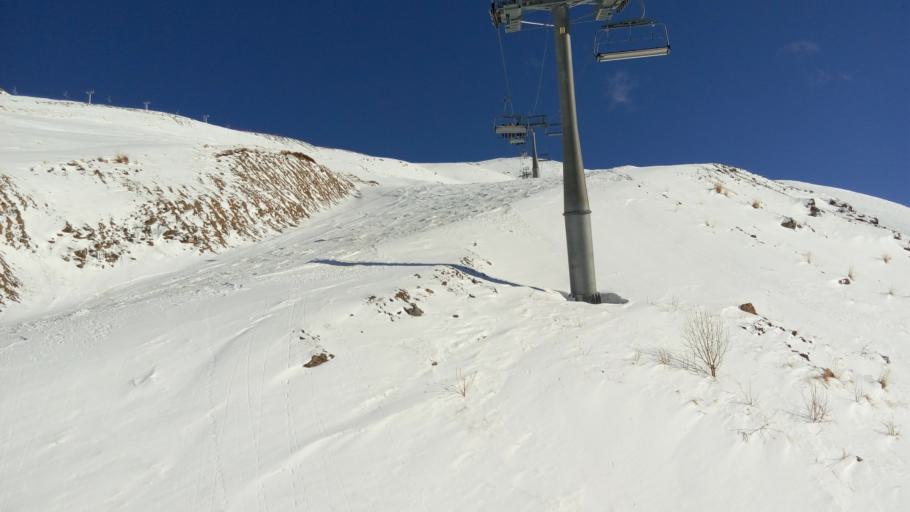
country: RU
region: Karachayevo-Cherkesiya
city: Teberda
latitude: 43.2912
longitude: 41.6588
